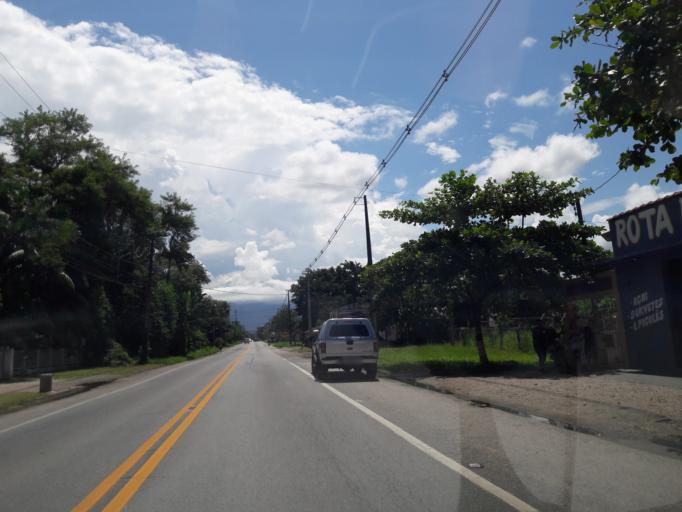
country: BR
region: Parana
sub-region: Antonina
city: Antonina
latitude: -25.4896
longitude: -48.8243
